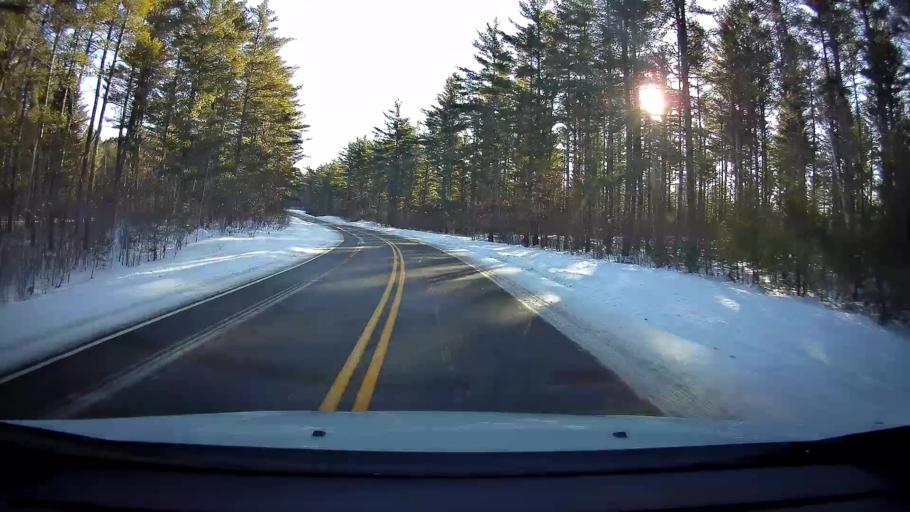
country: US
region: Wisconsin
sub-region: Sawyer County
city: Little Round Lake
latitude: 46.1122
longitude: -91.3151
